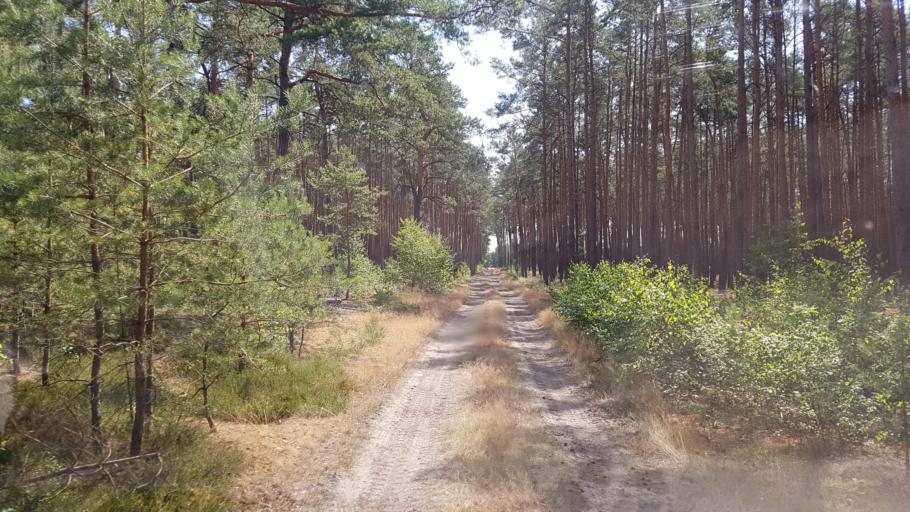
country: DE
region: Brandenburg
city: Finsterwalde
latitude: 51.6633
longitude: 13.7682
